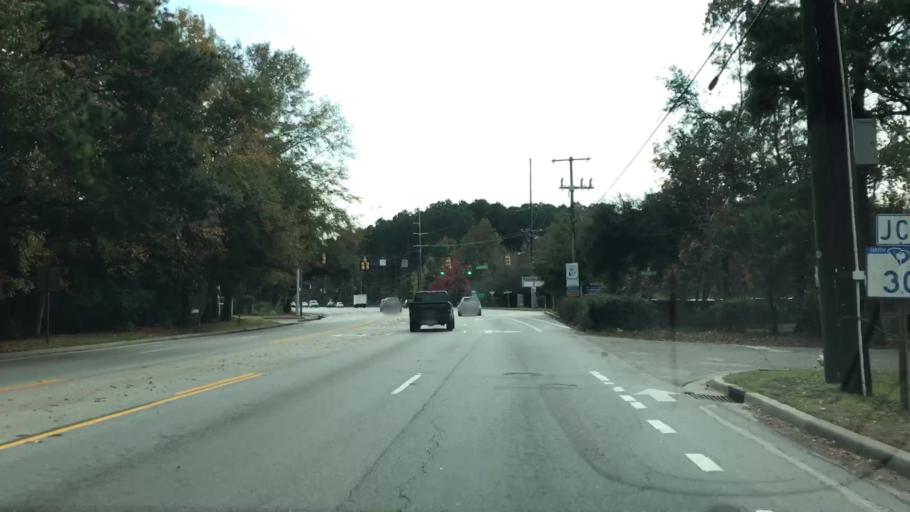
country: US
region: South Carolina
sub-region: Charleston County
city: Charleston
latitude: 32.7515
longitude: -79.9725
